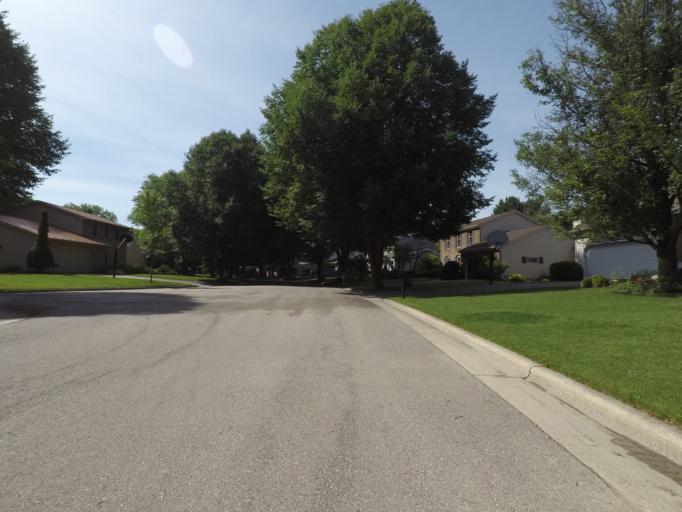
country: US
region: Wisconsin
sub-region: Dane County
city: Middleton
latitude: 43.0793
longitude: -89.5063
